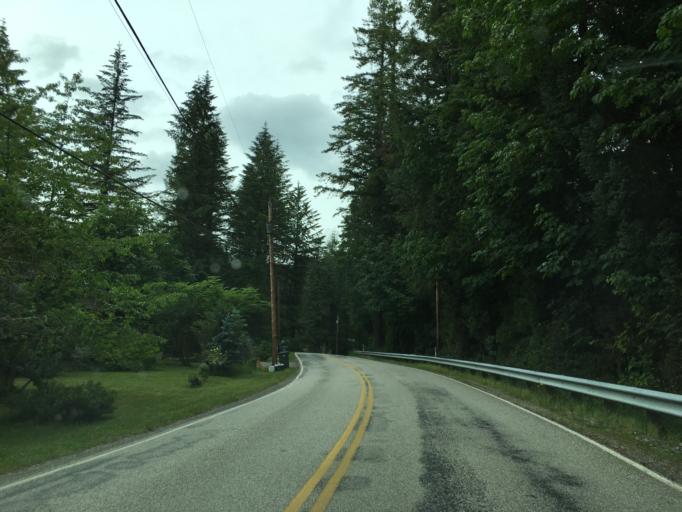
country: US
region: Washington
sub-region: Whatcom County
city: Peaceful Valley
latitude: 48.9265
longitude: -122.0778
